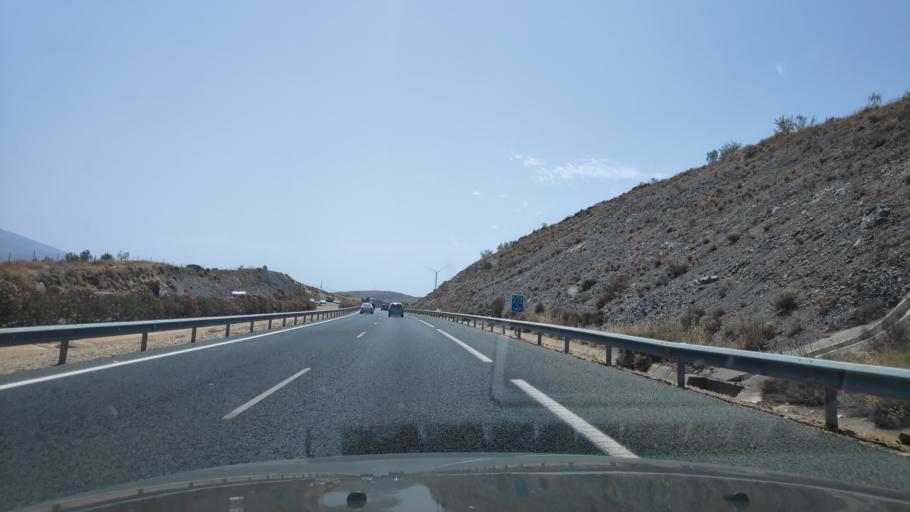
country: ES
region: Andalusia
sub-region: Provincia de Granada
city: Padul
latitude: 37.0217
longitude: -3.6434
